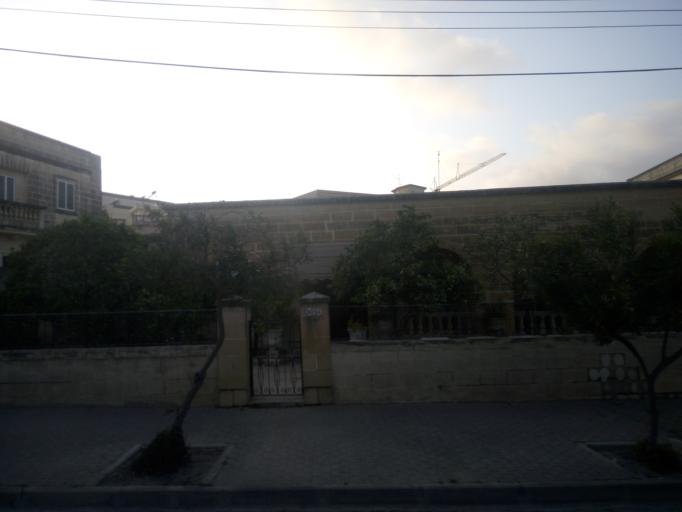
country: MT
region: Attard
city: Attard
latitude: 35.8910
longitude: 14.4457
